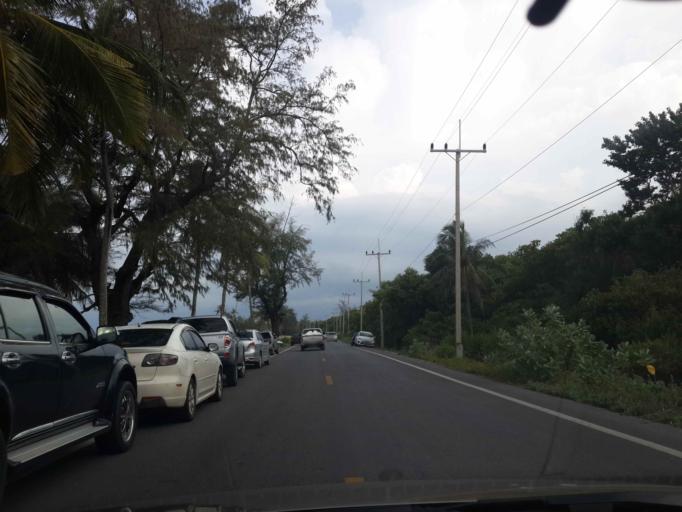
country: TH
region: Pattani
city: Yaring
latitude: 6.9121
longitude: 101.3432
